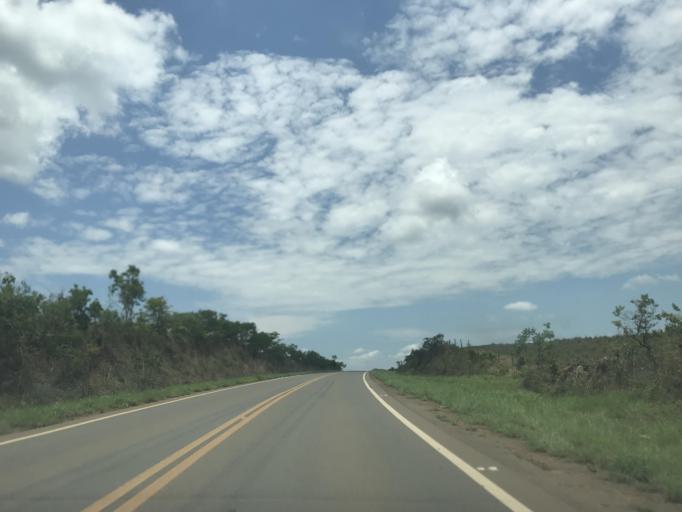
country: BR
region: Goias
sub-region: Luziania
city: Luziania
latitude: -16.4072
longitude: -48.1829
